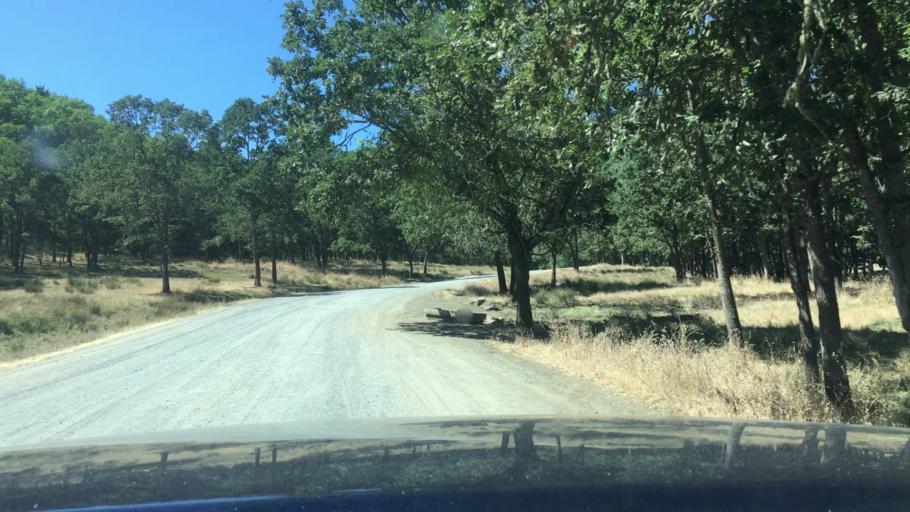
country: US
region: Oregon
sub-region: Douglas County
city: Winston
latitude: 43.1368
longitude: -123.4403
